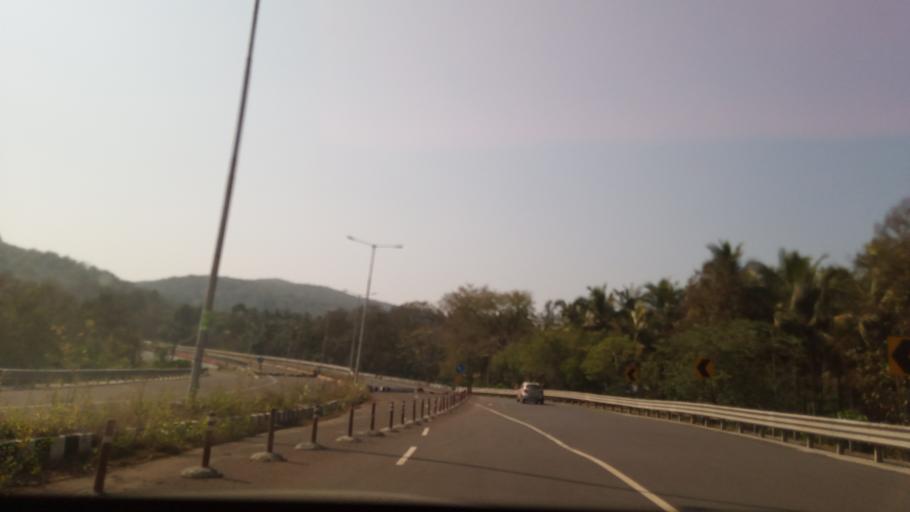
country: IN
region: Goa
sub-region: North Goa
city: Curti
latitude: 15.4239
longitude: 74.0483
